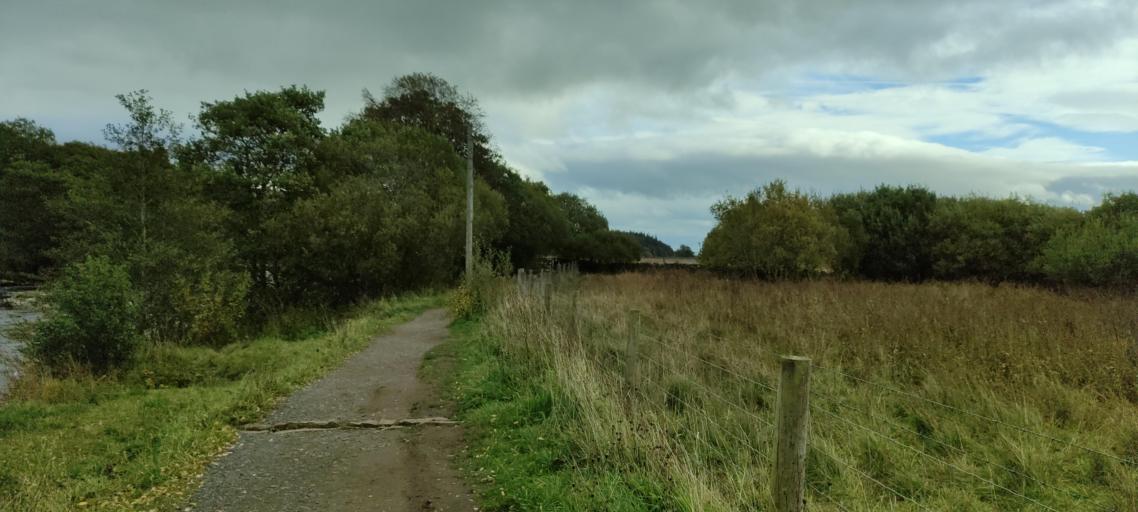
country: GB
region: England
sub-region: County Durham
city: Holwick
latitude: 54.6495
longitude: -2.1651
